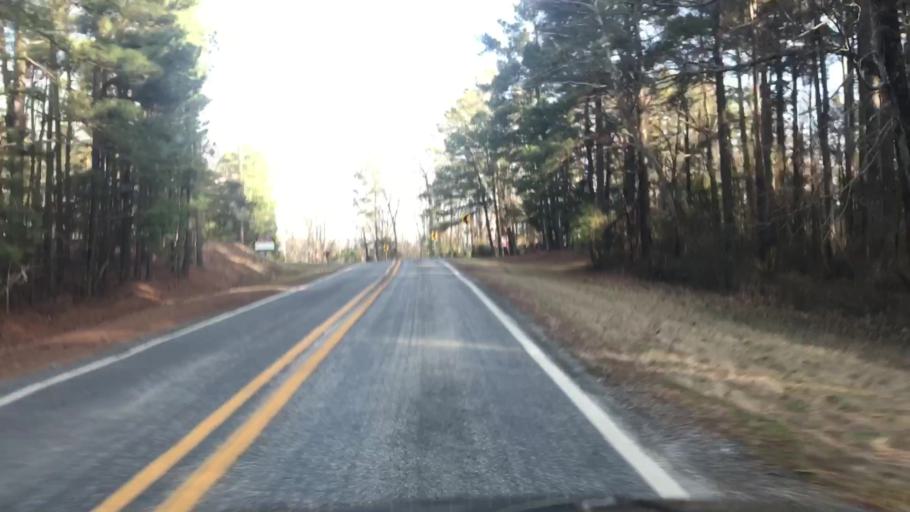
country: US
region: Arkansas
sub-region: Garland County
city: Rockwell
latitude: 34.4860
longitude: -93.2733
